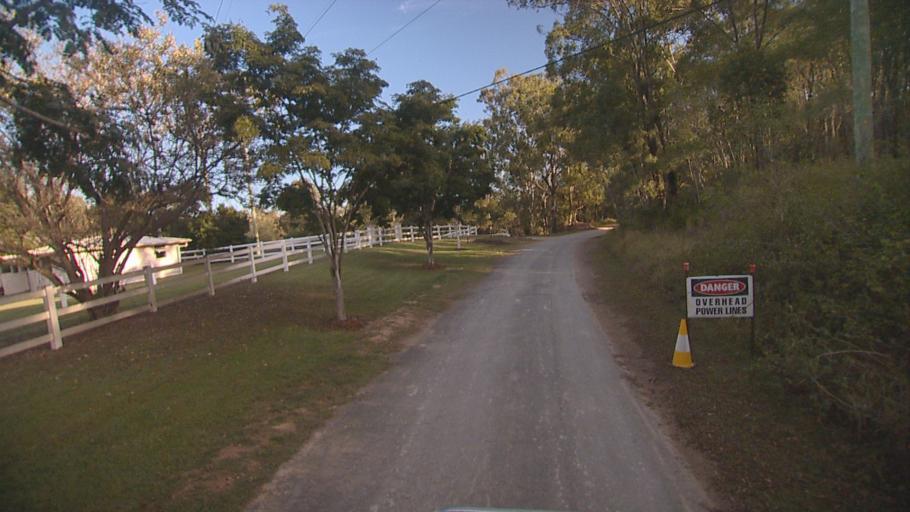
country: AU
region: Queensland
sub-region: Logan
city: Windaroo
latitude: -27.7931
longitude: 153.1793
